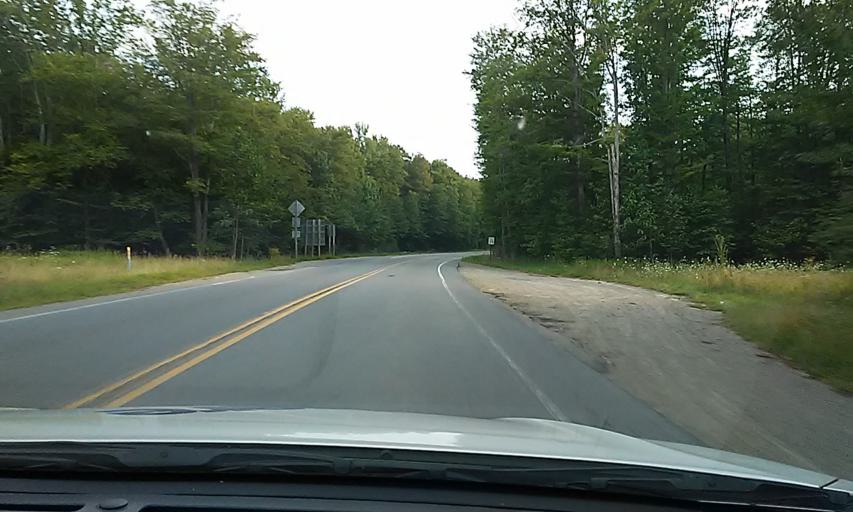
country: US
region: Pennsylvania
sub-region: McKean County
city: Kane
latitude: 41.6211
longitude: -78.8284
